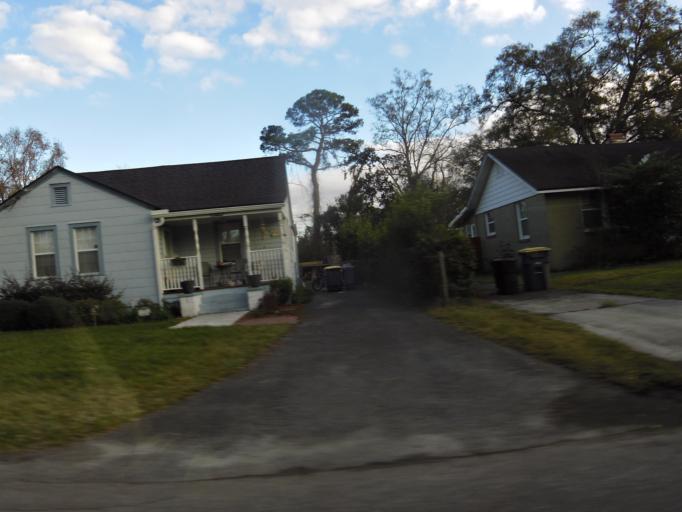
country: US
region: Florida
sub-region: Duval County
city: Jacksonville
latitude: 30.3113
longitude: -81.7104
